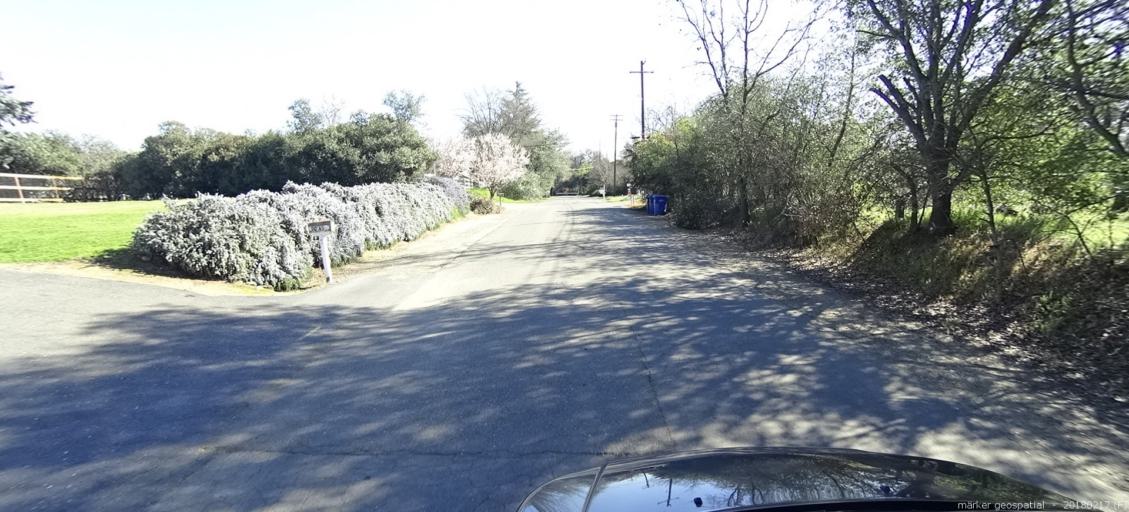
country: US
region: California
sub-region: Sacramento County
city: Orangevale
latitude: 38.7039
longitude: -121.2188
